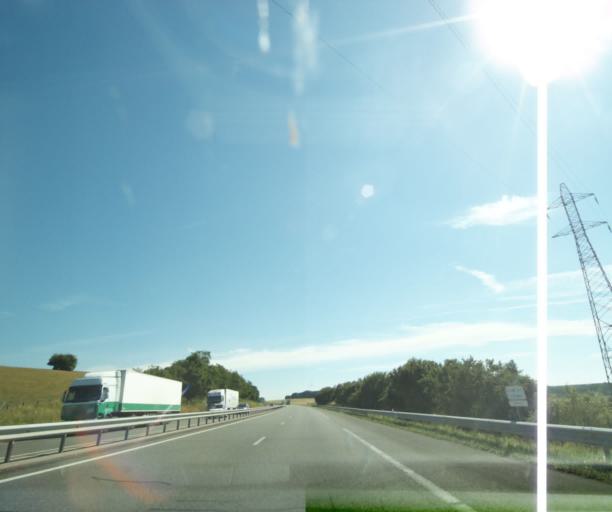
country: FR
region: Lorraine
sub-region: Departement des Vosges
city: Bulgneville
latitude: 48.1938
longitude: 5.7790
